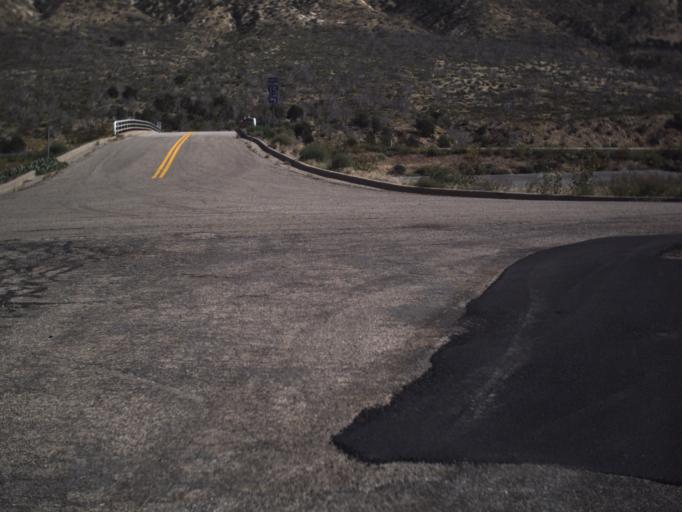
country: US
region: Utah
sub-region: Washington County
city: Toquerville
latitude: 37.3621
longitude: -113.2636
